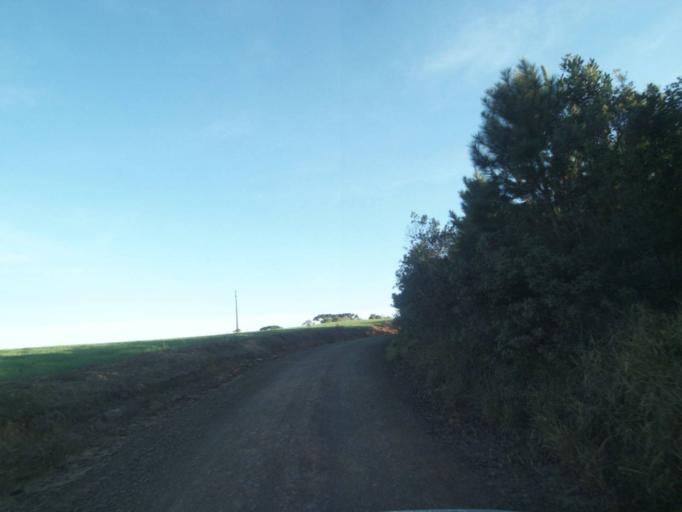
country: BR
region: Parana
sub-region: Telemaco Borba
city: Telemaco Borba
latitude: -24.4299
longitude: -50.5970
